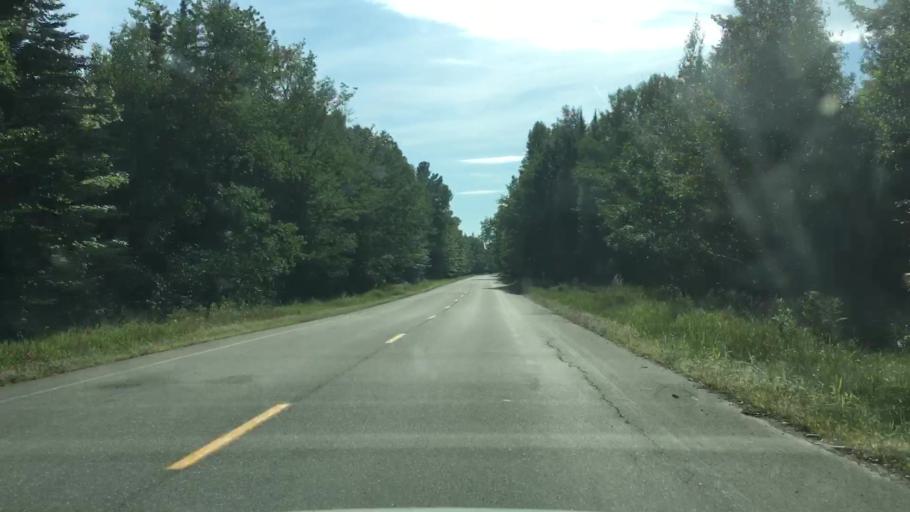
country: US
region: Maine
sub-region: Penobscot County
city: Lincoln
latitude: 45.3859
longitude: -68.5395
